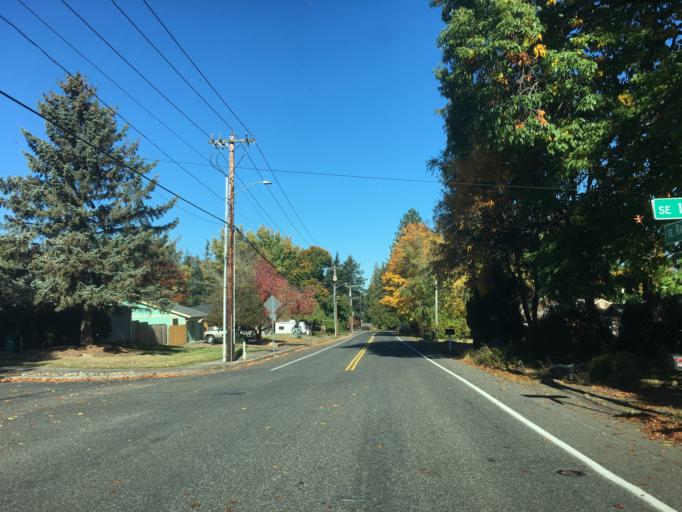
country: US
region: Oregon
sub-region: Multnomah County
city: Gresham
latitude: 45.4832
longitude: -122.4230
